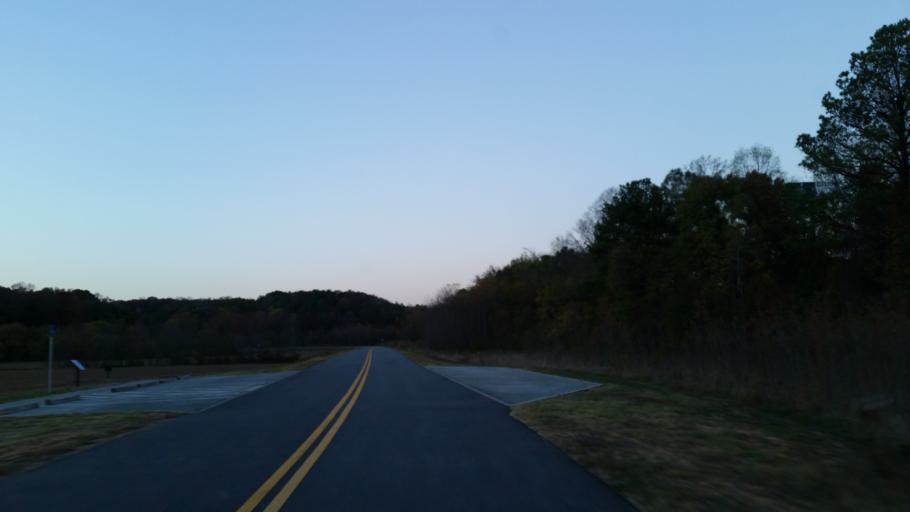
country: US
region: Georgia
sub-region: Gordon County
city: Calhoun
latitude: 34.5814
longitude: -84.9528
